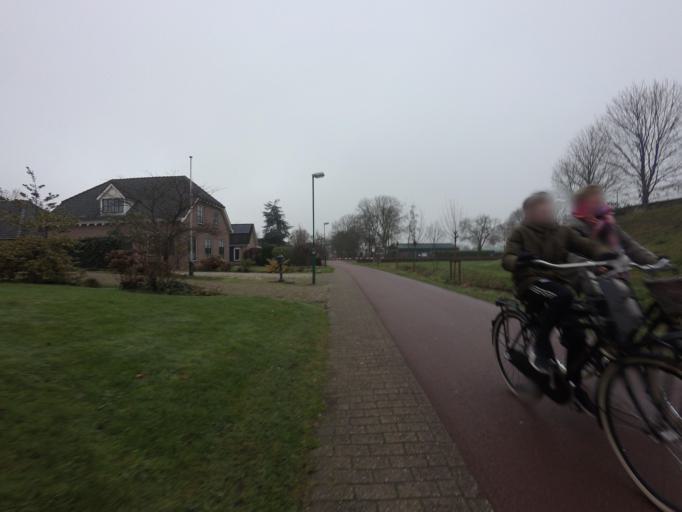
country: NL
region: Utrecht
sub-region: Gemeente Houten
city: Houten
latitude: 52.0220
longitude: 5.1577
